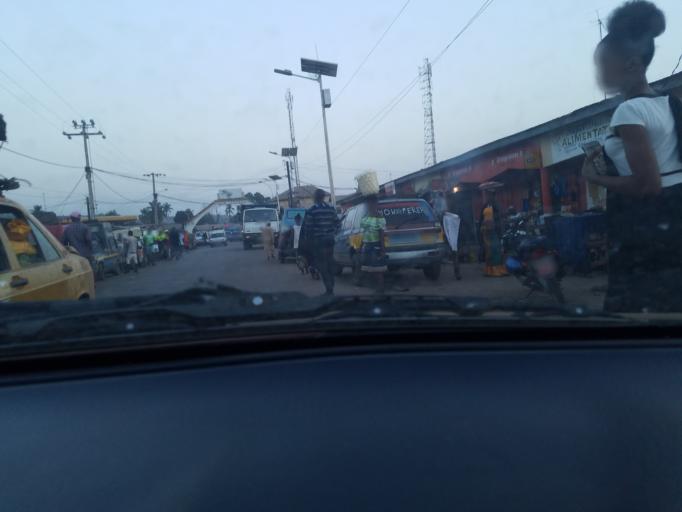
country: GN
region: Kindia
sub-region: Prefecture de Dubreka
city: Dubreka
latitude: 9.7871
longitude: -13.4874
